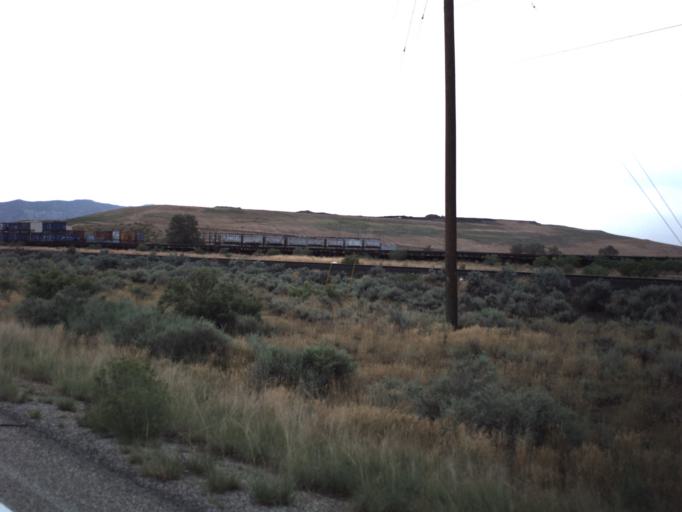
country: US
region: Utah
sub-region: Carbon County
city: East Carbon City
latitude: 39.5356
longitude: -110.4862
